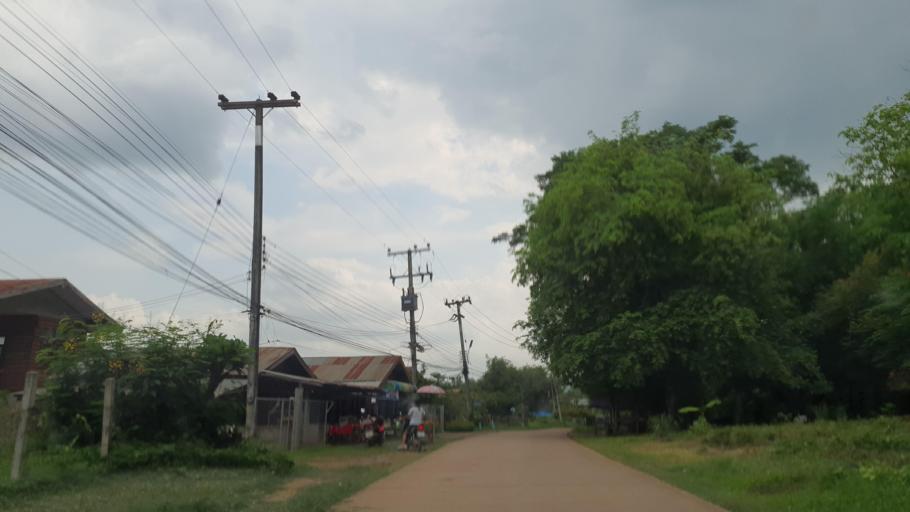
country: TH
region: Sukhothai
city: Thung Saliam
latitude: 17.3153
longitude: 99.5094
